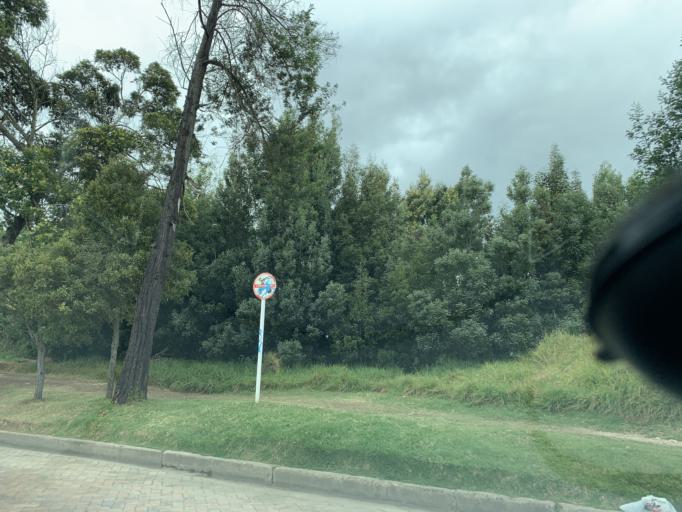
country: CO
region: Boyaca
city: Tunja
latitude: 5.5564
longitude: -73.3480
